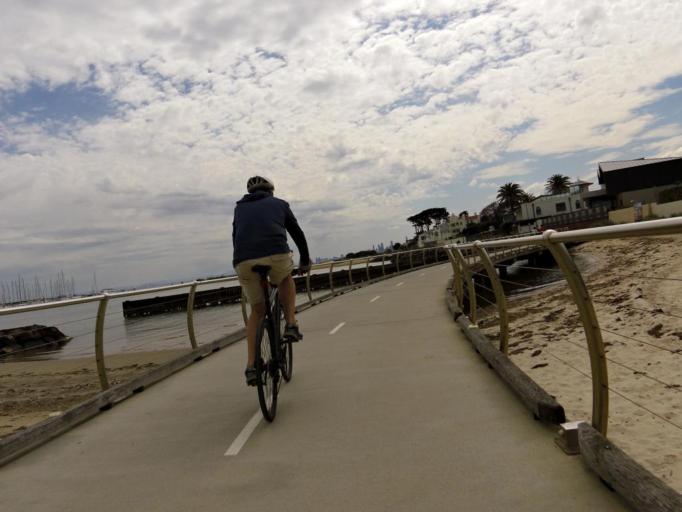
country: AU
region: Victoria
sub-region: Bayside
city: North Brighton
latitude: -37.9085
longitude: 144.9854
